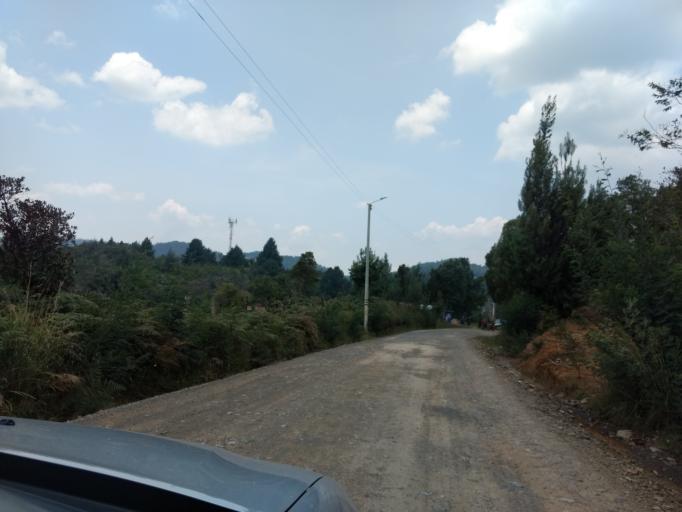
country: CO
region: Boyaca
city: Raquira
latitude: 5.5127
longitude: -73.7193
